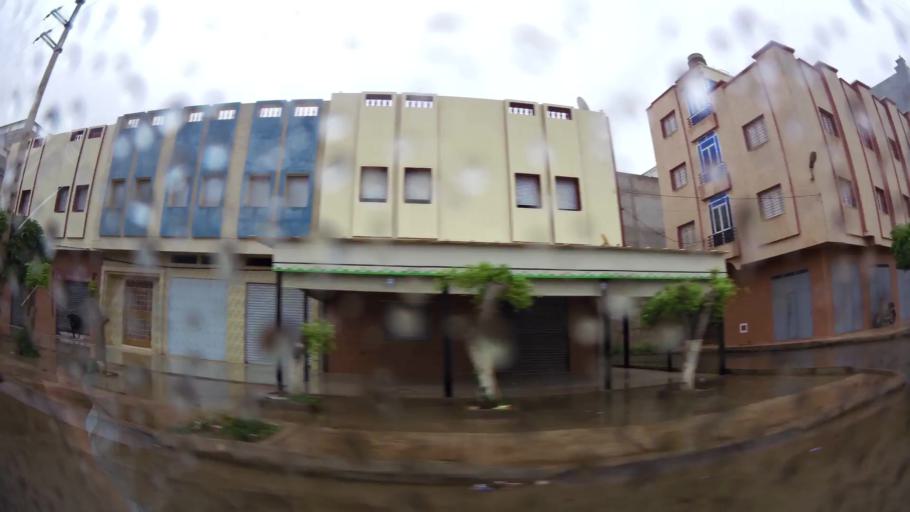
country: MA
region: Oriental
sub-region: Nador
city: Boudinar
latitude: 35.1168
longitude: -3.6438
